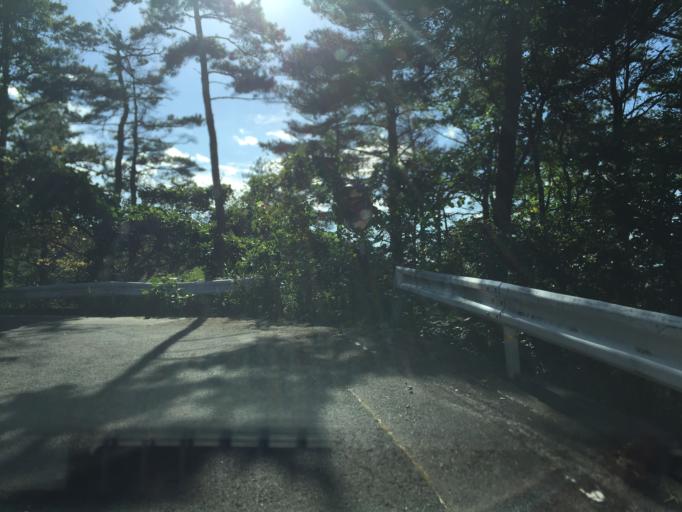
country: JP
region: Fukushima
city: Yanagawamachi-saiwaicho
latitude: 37.8470
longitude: 140.6839
